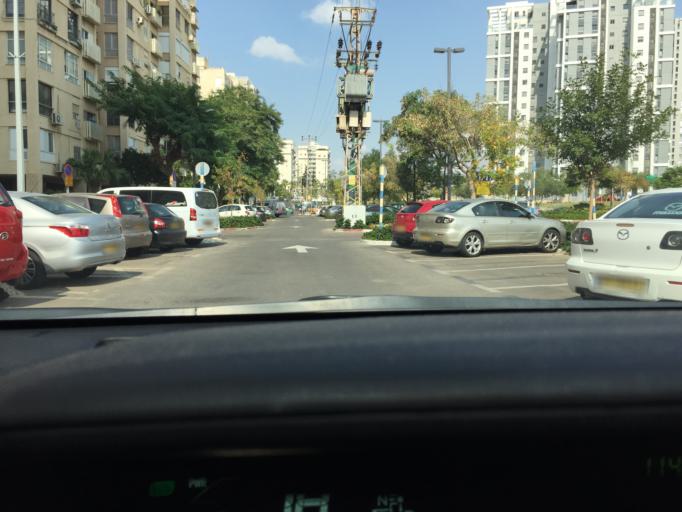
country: IL
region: Tel Aviv
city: Giv`at Shemu'el
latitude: 32.0668
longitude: 34.8467
